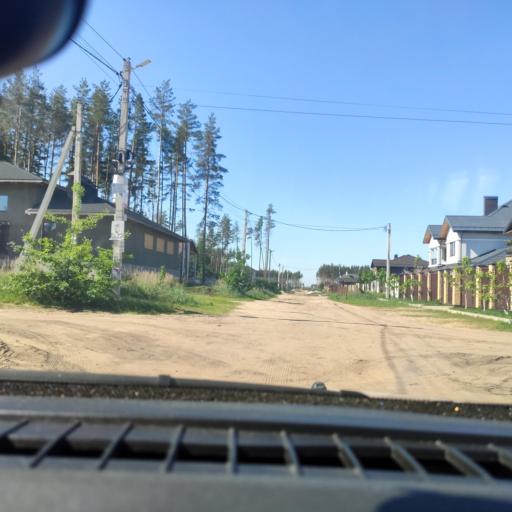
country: RU
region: Voronezj
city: Podgornoye
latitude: 51.7811
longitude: 39.1470
